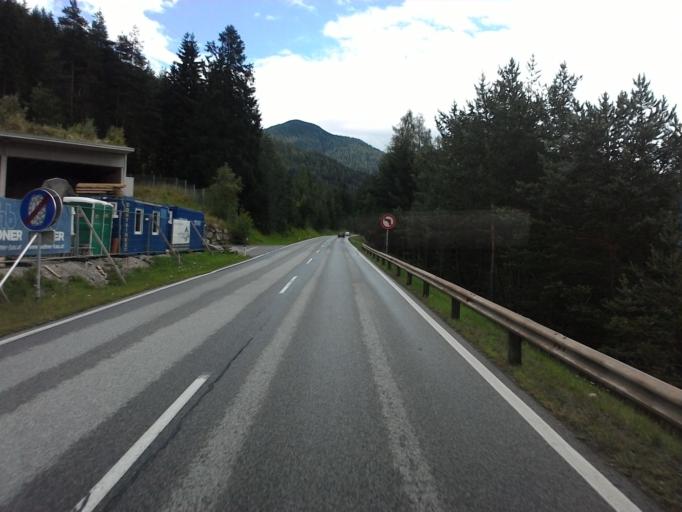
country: AT
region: Tyrol
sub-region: Politischer Bezirk Innsbruck Land
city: Seefeld in Tirol
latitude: 47.3342
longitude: 11.1963
